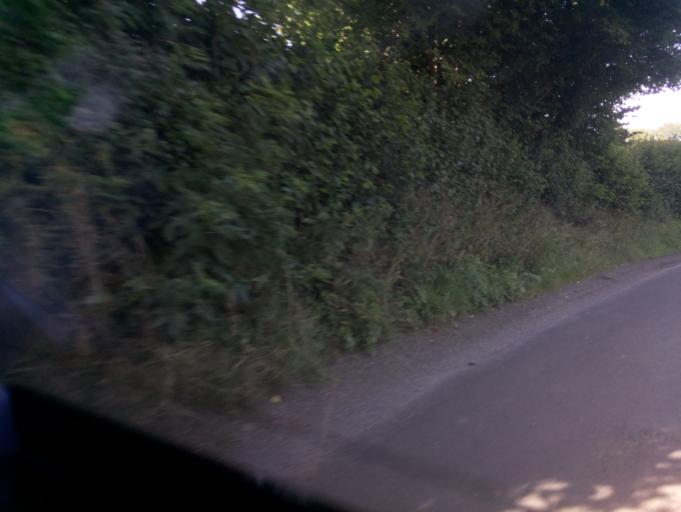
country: GB
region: England
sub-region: South Gloucestershire
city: Bitton
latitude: 51.4334
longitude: -2.4155
